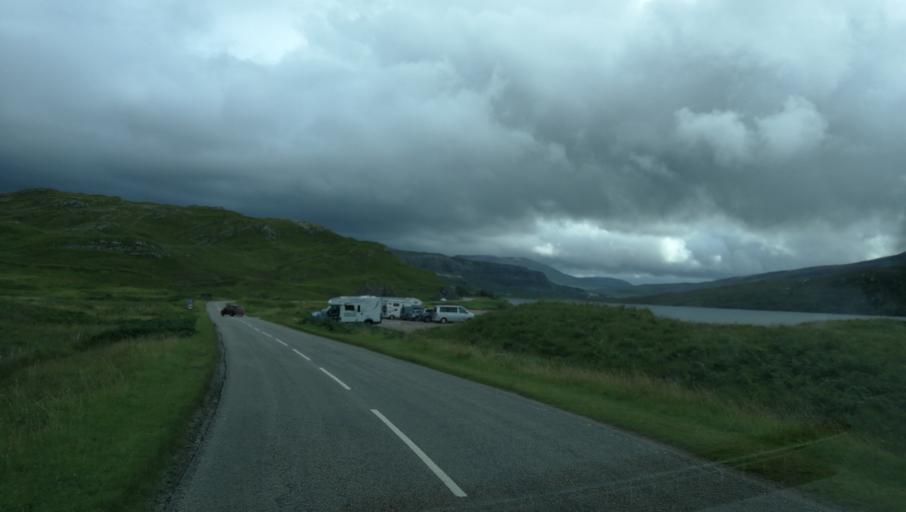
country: GB
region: Scotland
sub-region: Highland
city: Ullapool
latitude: 58.1666
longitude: -4.9893
